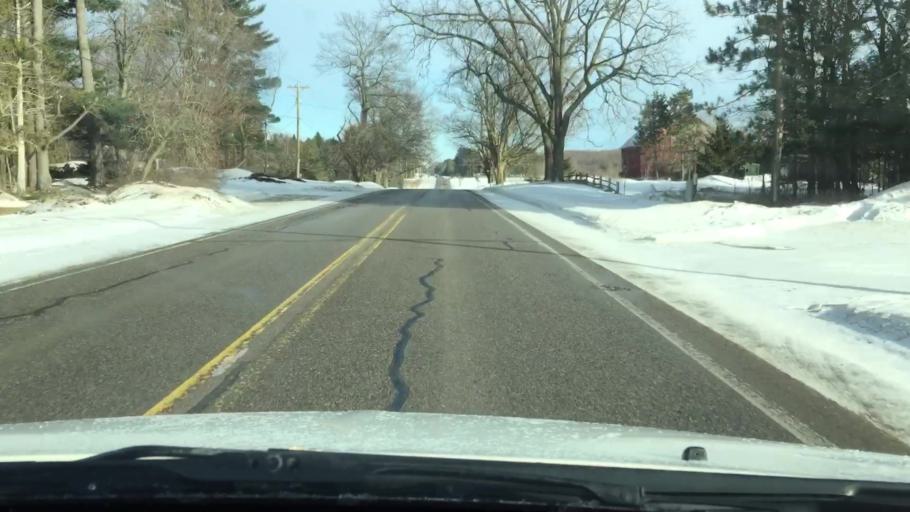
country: US
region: Michigan
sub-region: Kalkaska County
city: Kalkaska
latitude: 44.6410
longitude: -85.2584
